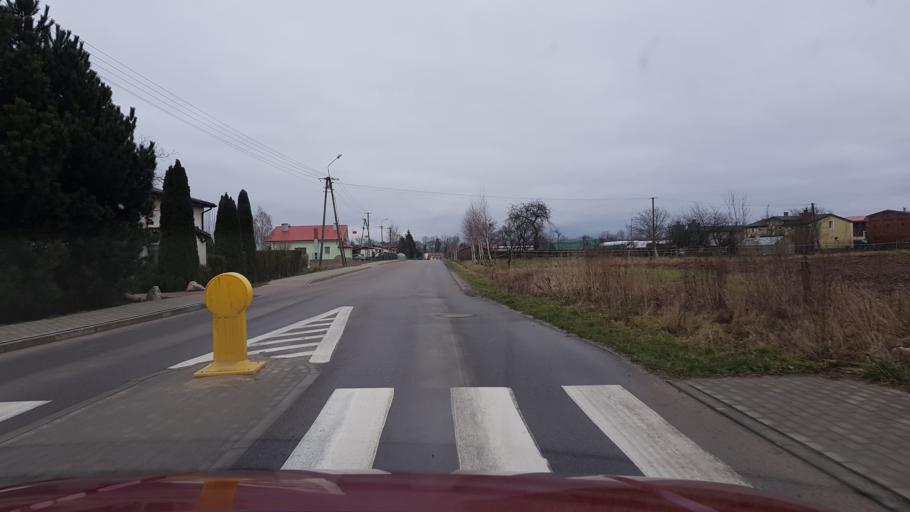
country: PL
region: West Pomeranian Voivodeship
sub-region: Powiat koszalinski
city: Mielno
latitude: 54.1672
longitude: 16.0289
